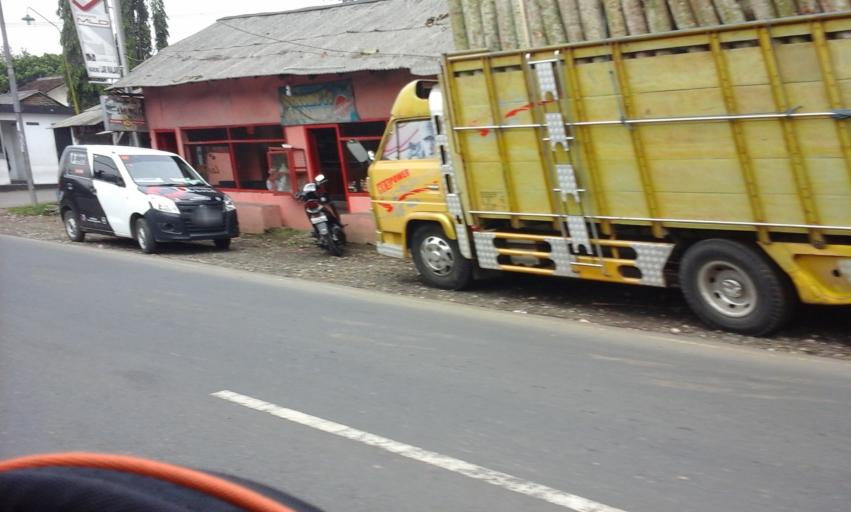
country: ID
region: East Java
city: Gambirono
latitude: -8.2000
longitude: 113.5242
